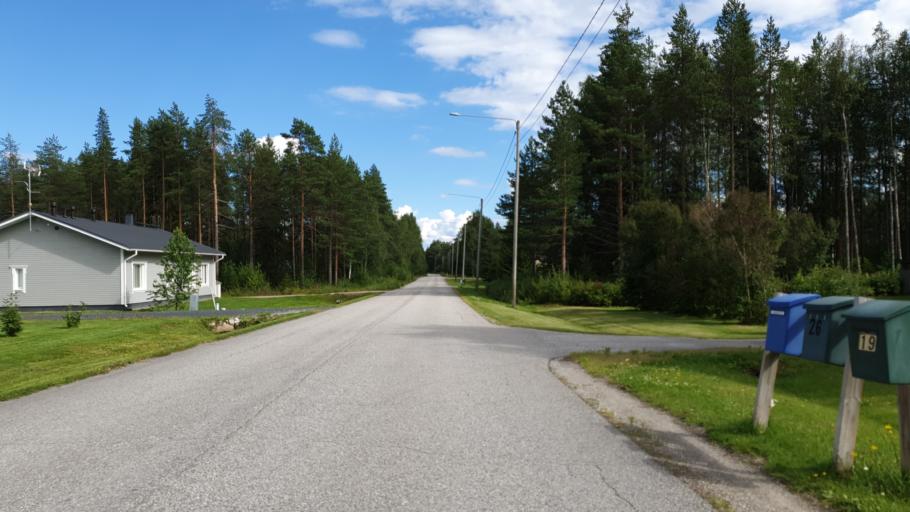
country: FI
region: Kainuu
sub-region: Kehys-Kainuu
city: Kuhmo
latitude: 64.1193
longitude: 29.5572
